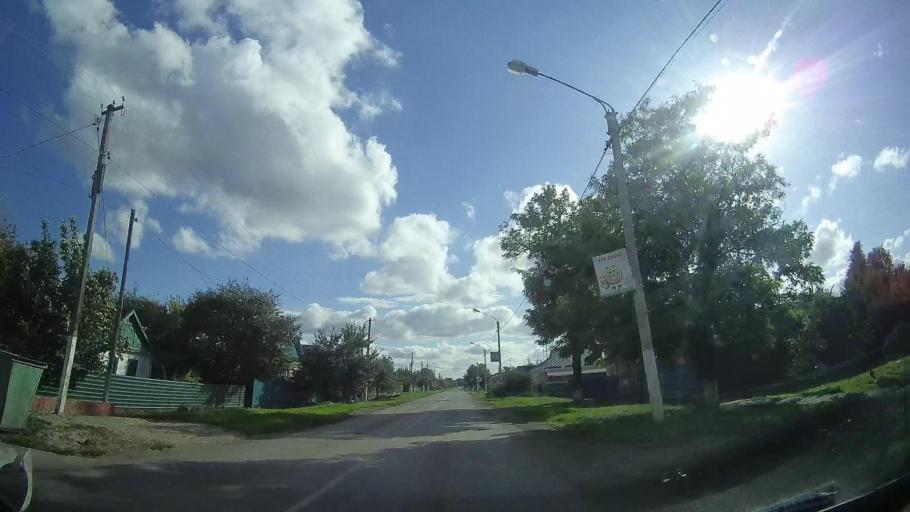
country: RU
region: Rostov
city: Tselina
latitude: 46.5364
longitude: 41.0340
